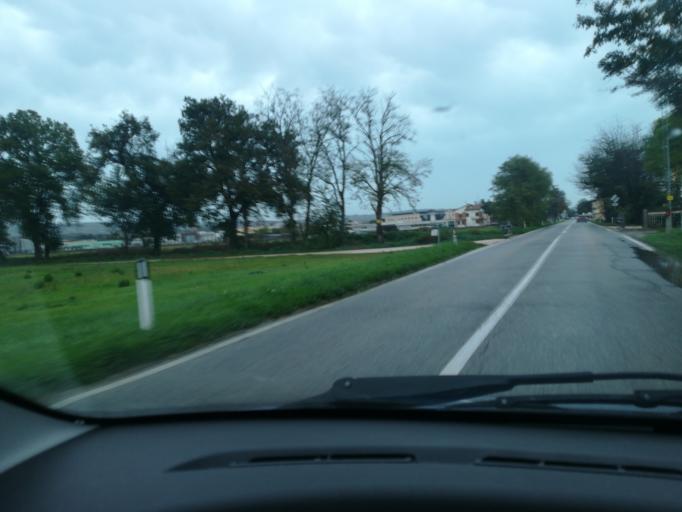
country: IT
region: The Marches
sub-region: Provincia di Macerata
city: Borgo Stazione
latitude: 43.2801
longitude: 13.6259
